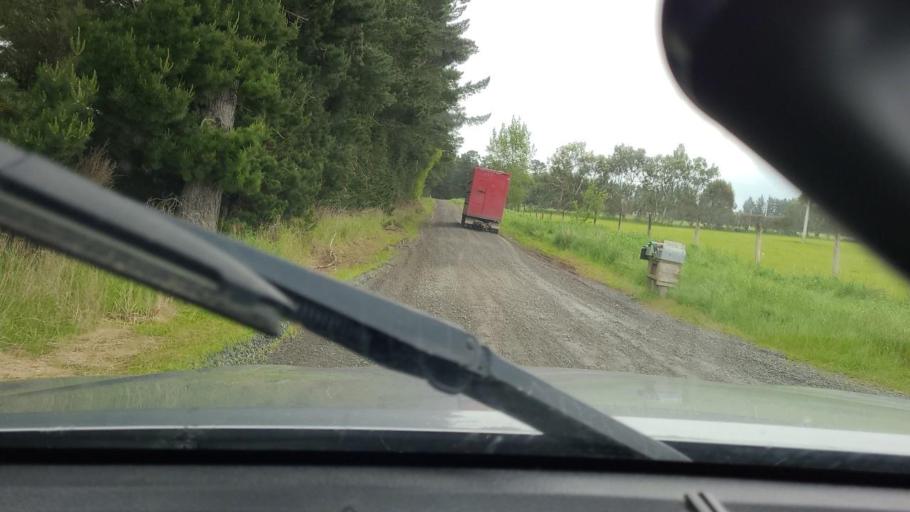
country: NZ
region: Southland
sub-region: Southland District
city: Winton
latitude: -45.7803
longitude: 168.1819
